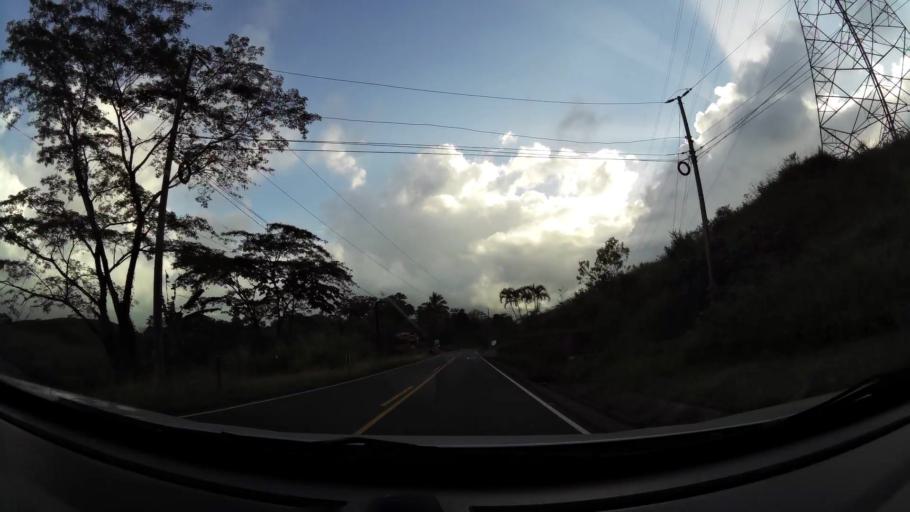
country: CR
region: Limon
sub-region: Canton de Siquirres
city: Siquirres
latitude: 10.0155
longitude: -83.5640
